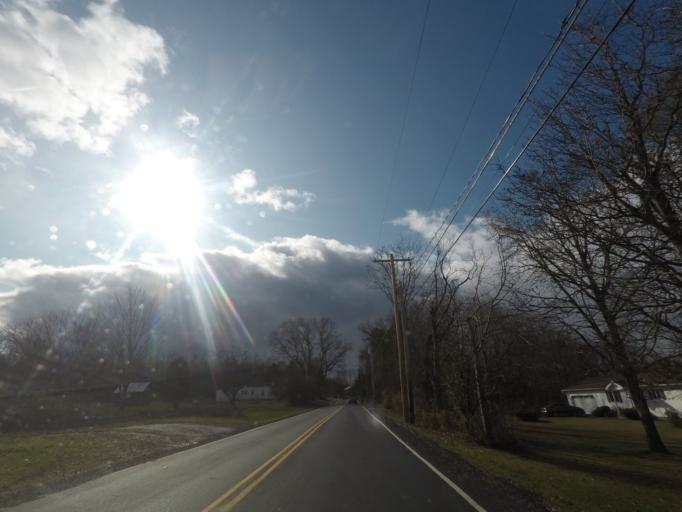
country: US
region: New York
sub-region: Saratoga County
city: Country Knolls
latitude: 42.9343
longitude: -73.8528
